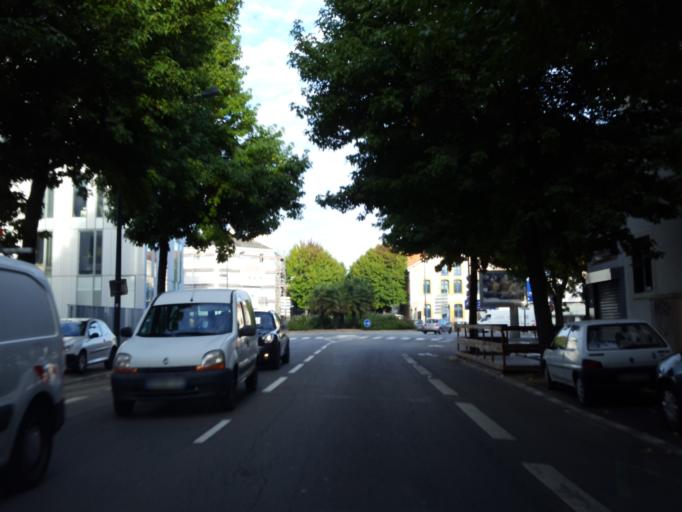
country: FR
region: Pays de la Loire
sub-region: Departement de la Loire-Atlantique
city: Nantes
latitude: 47.2035
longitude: -1.5509
